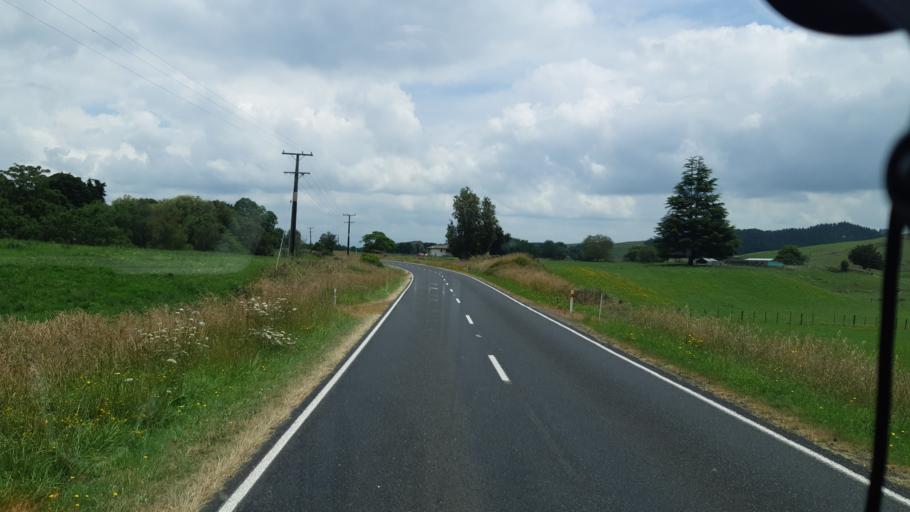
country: NZ
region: Waikato
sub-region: Waipa District
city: Cambridge
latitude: -38.1064
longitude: 175.4923
